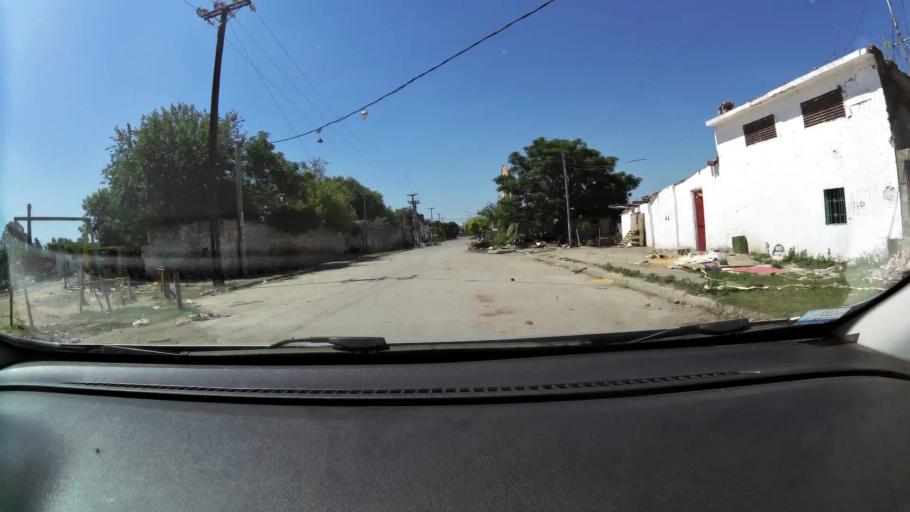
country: AR
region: Cordoba
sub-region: Departamento de Capital
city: Cordoba
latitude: -31.3914
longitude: -64.1912
